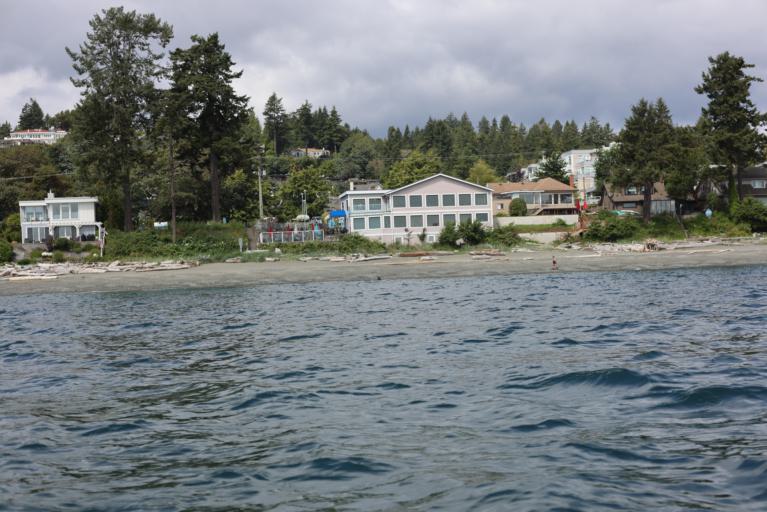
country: CA
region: British Columbia
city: Victoria
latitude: 48.5214
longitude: -123.3646
